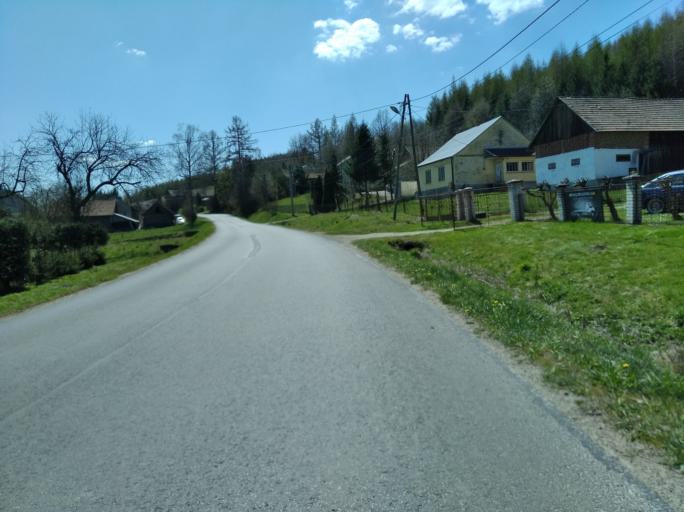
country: PL
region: Subcarpathian Voivodeship
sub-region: Powiat brzozowski
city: Dydnia
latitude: 49.6926
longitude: 22.1838
